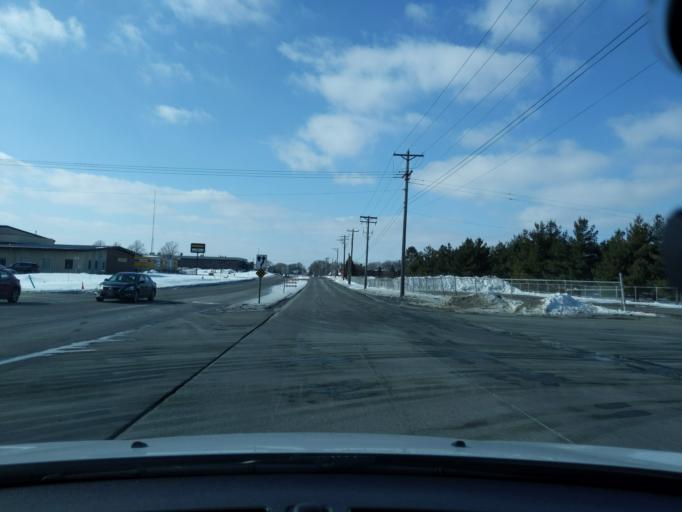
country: US
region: Minnesota
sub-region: Hennepin County
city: Saint Anthony
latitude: 45.0207
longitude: -93.2032
